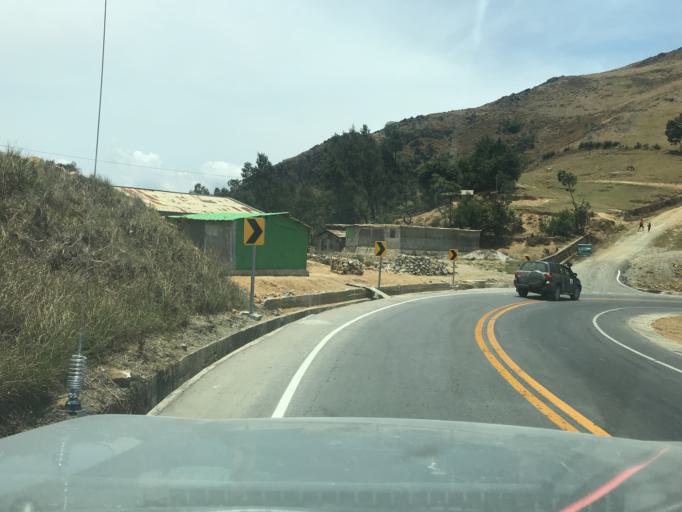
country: TL
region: Manufahi
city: Same
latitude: -8.8777
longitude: 125.6043
